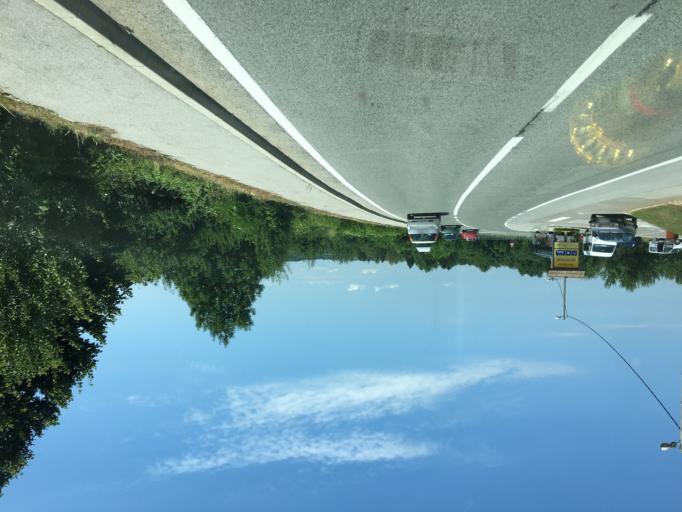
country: HR
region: Licko-Senjska
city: Jezerce
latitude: 44.9447
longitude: 15.6366
